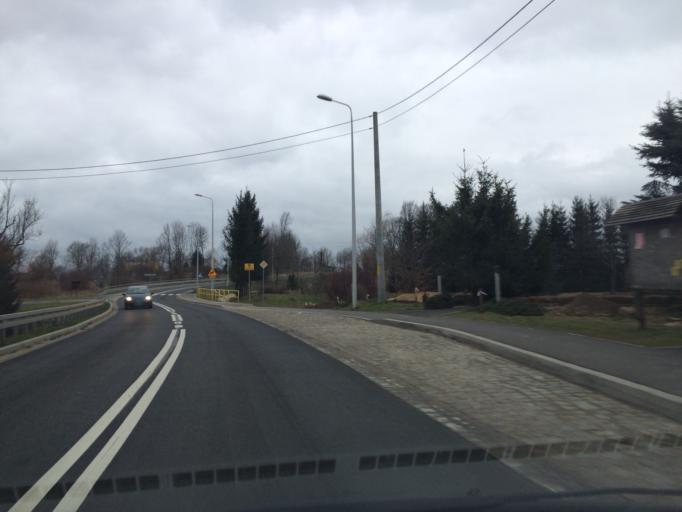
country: PL
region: Lower Silesian Voivodeship
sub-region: Powiat lubanski
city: Pisarzowice
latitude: 51.1670
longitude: 15.2646
